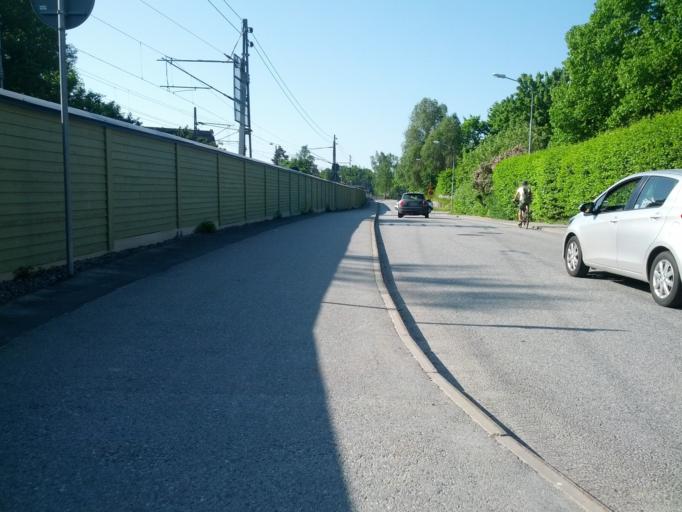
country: SE
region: Stockholm
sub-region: Danderyds Kommun
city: Djursholm
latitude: 59.4014
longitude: 18.0591
